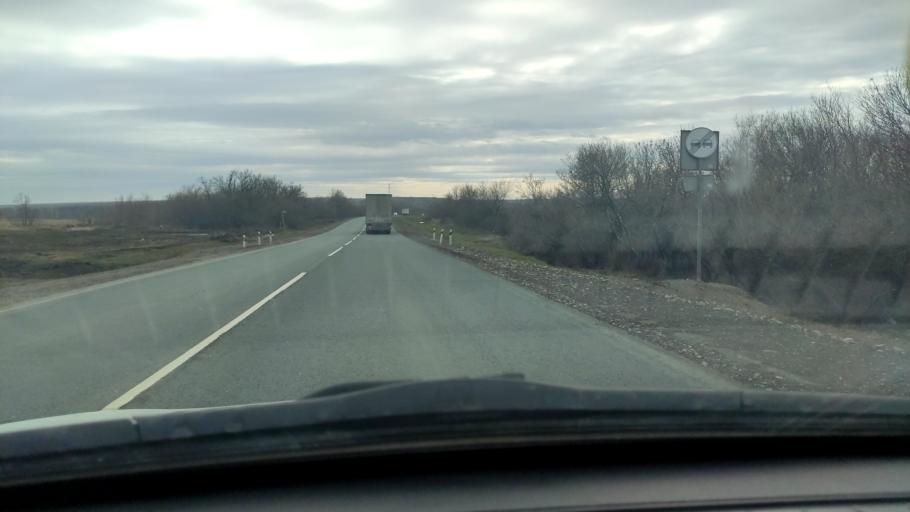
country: RU
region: Samara
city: Zhigulevsk
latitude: 53.3054
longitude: 49.3498
